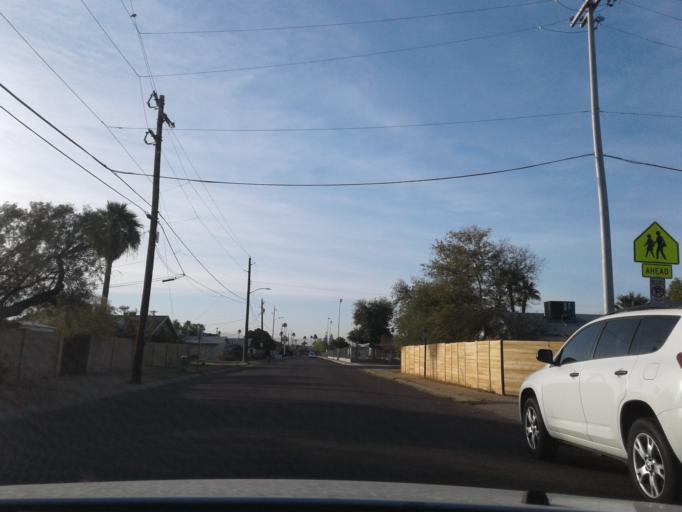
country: US
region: Arizona
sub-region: Maricopa County
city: Phoenix
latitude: 33.4919
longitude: -112.0870
